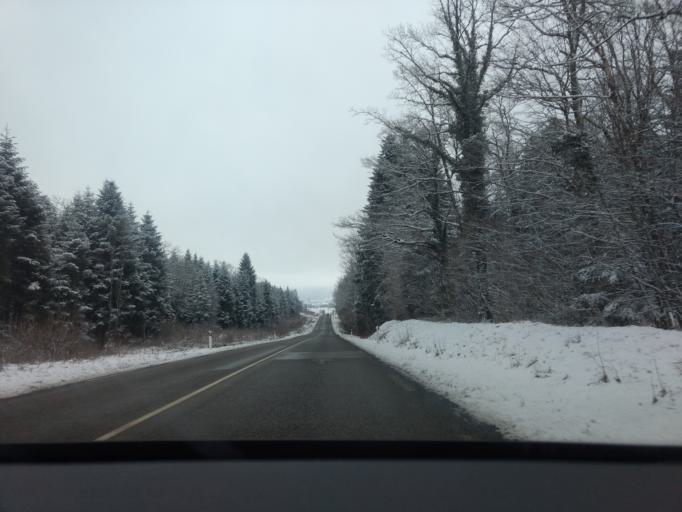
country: FR
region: Franche-Comte
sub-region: Departement du Jura
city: Champagnole
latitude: 46.7808
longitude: 5.8789
